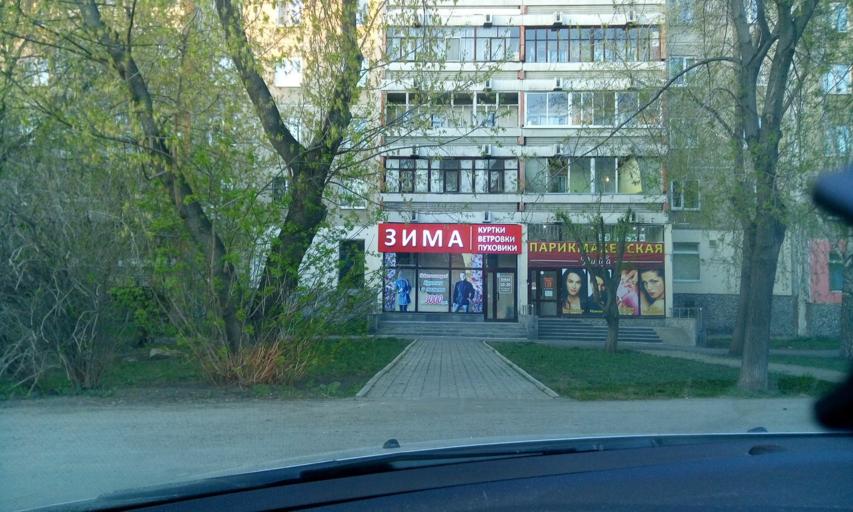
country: RU
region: Sverdlovsk
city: Yekaterinburg
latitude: 56.8362
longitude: 60.6814
